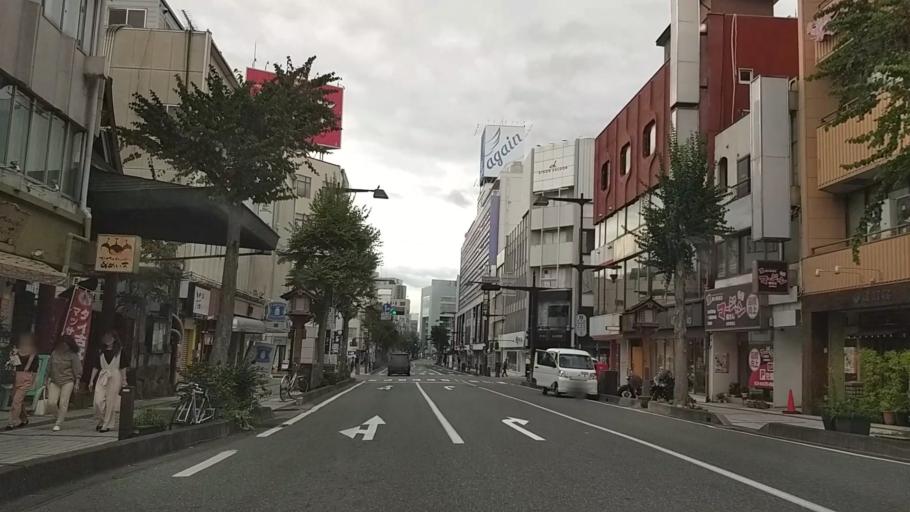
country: JP
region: Nagano
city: Nagano-shi
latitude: 36.6475
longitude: 138.1871
